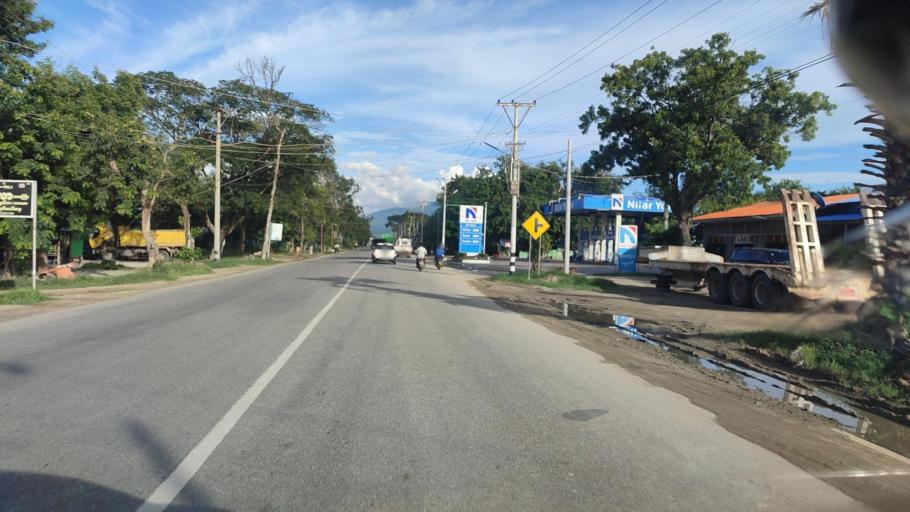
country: MM
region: Mandalay
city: Yamethin
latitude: 20.1171
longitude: 96.2194
